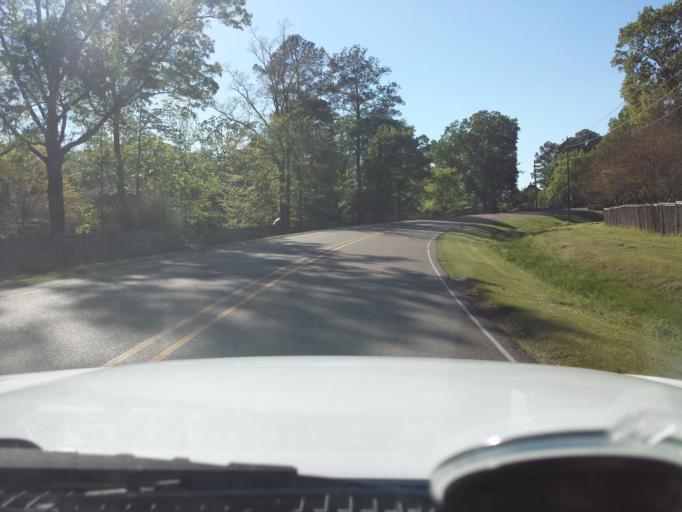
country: US
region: Mississippi
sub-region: Madison County
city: Madison
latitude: 32.4136
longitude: -90.0189
